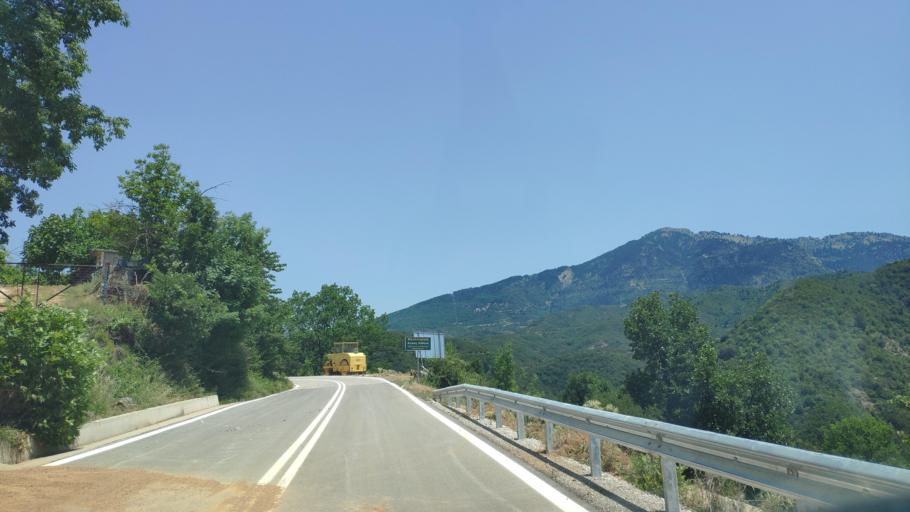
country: GR
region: Epirus
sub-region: Nomos Artas
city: Ano Kalentini
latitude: 39.1936
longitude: 21.3517
